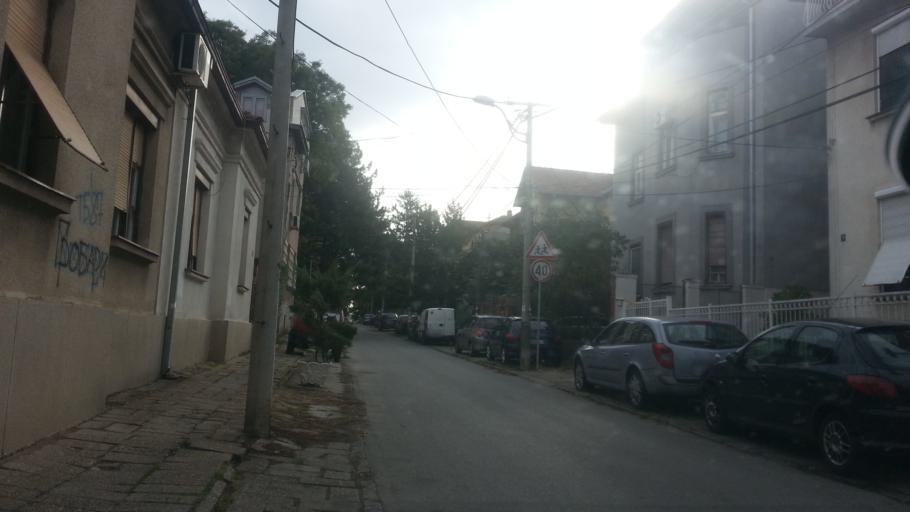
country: RS
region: Central Serbia
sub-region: Belgrade
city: Zemun
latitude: 44.8404
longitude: 20.3998
